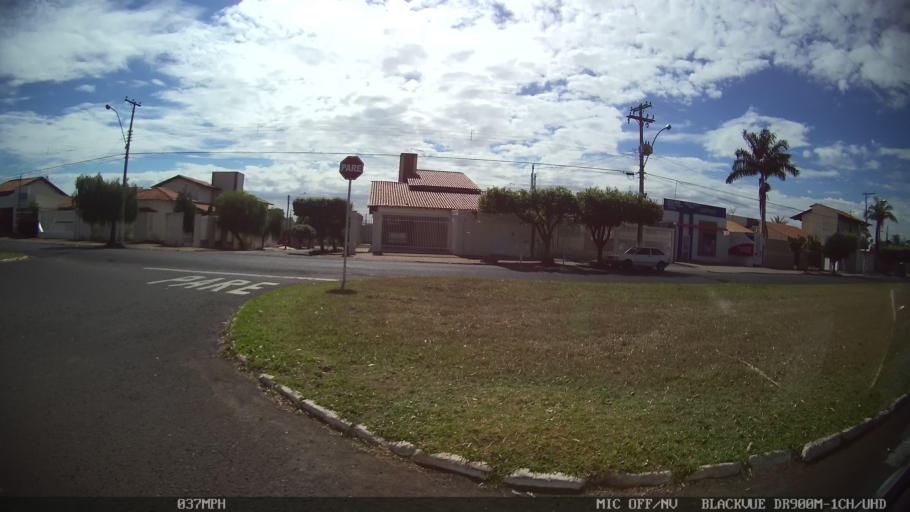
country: BR
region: Sao Paulo
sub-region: Bady Bassitt
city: Bady Bassitt
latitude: -20.8138
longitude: -49.4989
